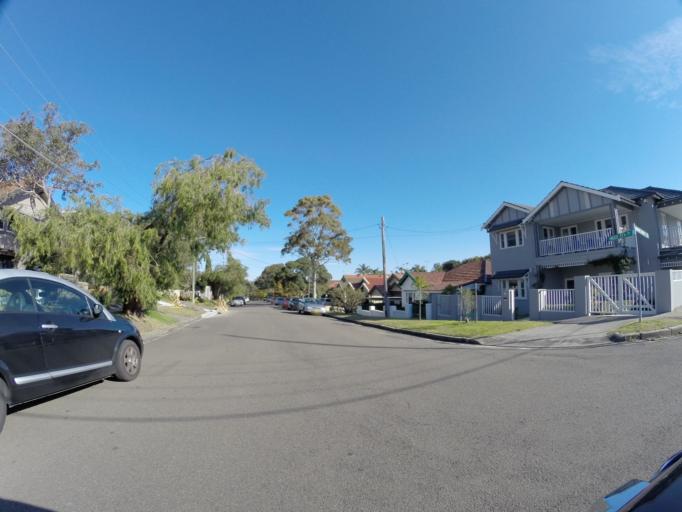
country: AU
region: New South Wales
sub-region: Randwick
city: Coogee
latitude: -33.9240
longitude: 151.2483
